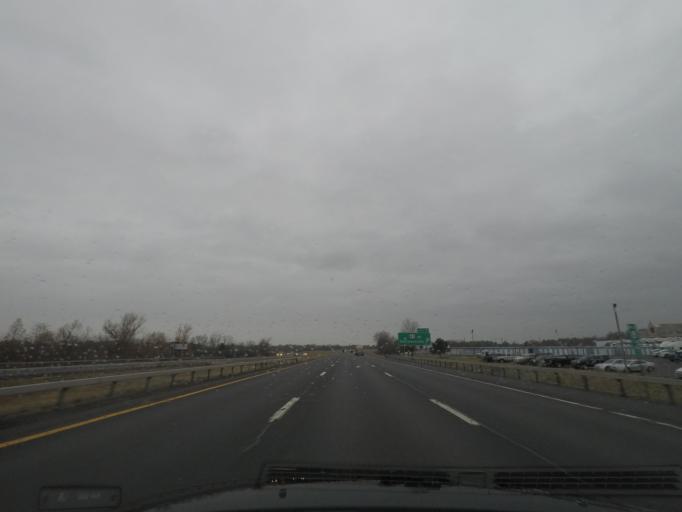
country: US
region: New York
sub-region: Rensselaer County
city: Hampton Manor
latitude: 42.6448
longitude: -73.7105
